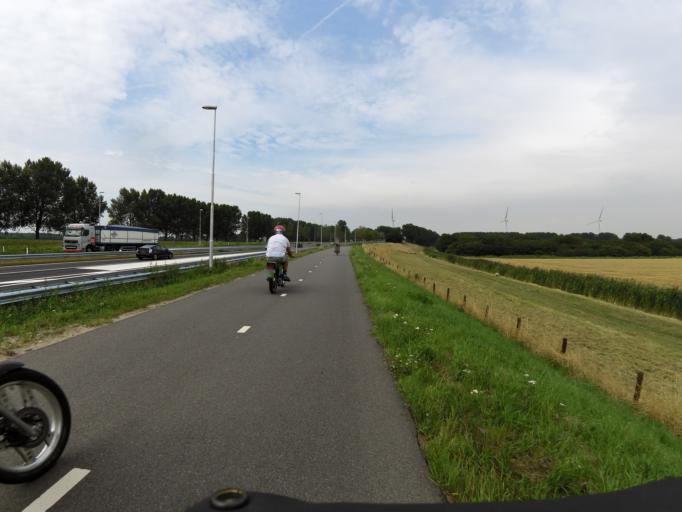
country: NL
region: South Holland
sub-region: Gemeente Brielle
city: Brielle
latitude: 51.8939
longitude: 4.1998
